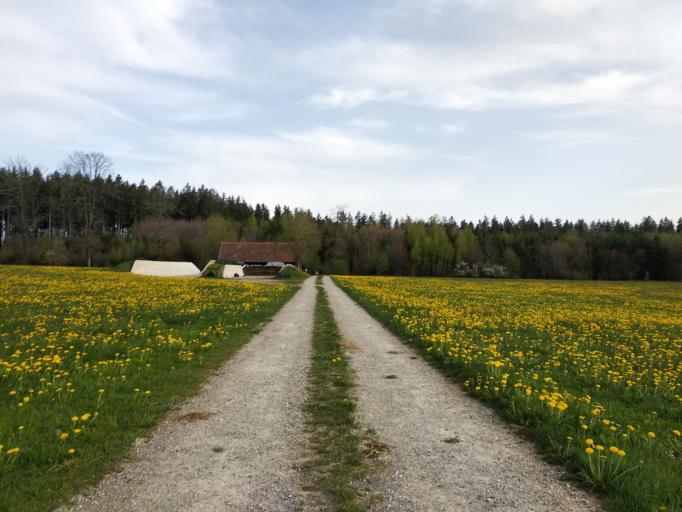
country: DE
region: Bavaria
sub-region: Swabia
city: Kronburg
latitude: 47.9034
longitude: 10.1518
